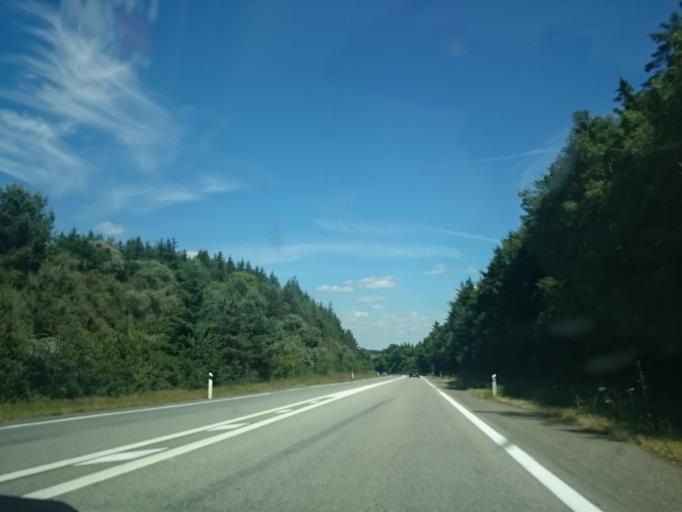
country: FR
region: Brittany
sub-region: Departement des Cotes-d'Armor
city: Mur-de-Bretagne
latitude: 48.2184
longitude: -3.0373
